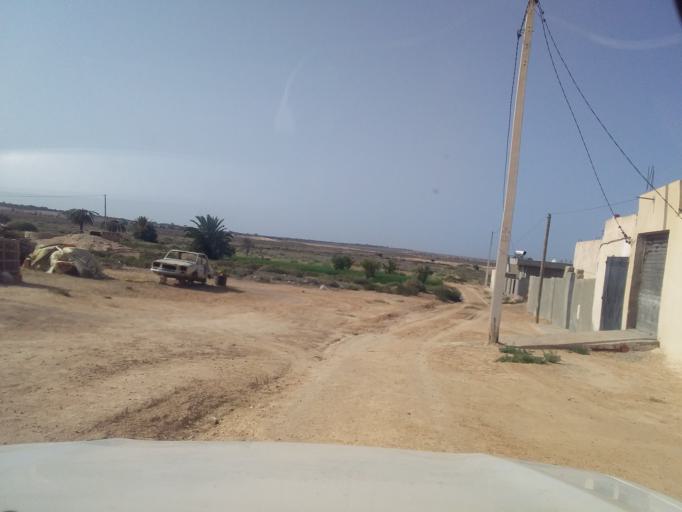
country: TN
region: Qabis
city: Gabes
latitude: 33.6426
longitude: 10.2953
